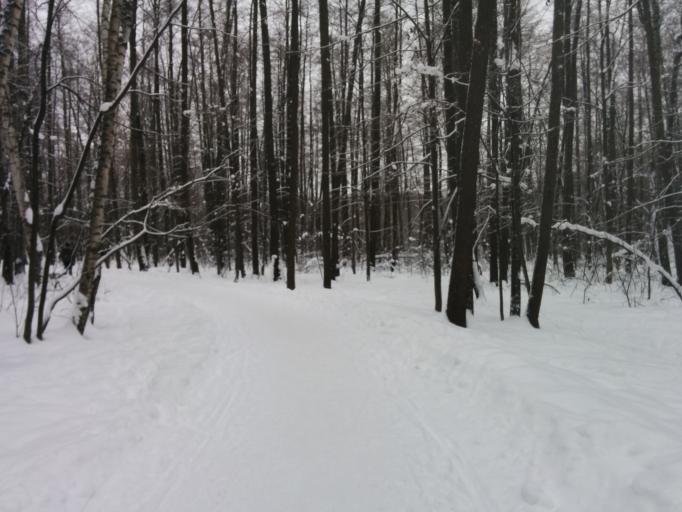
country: RU
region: Moskovskaya
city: Izmaylovo
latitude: 55.7864
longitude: 37.7797
